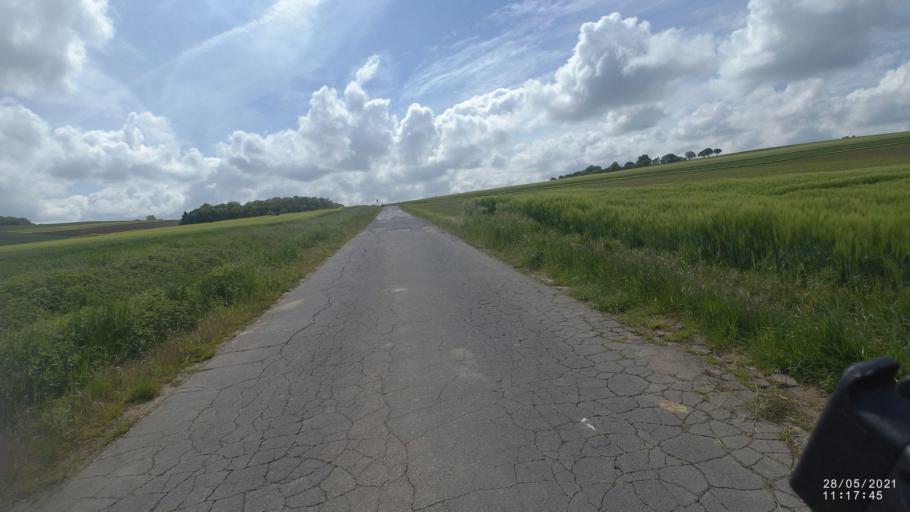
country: DE
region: Rheinland-Pfalz
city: Wierschem
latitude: 50.2304
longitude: 7.3392
